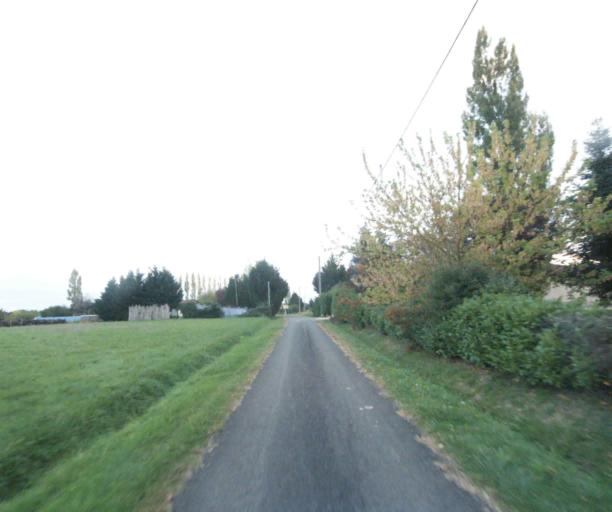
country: FR
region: Midi-Pyrenees
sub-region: Departement du Gers
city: Montreal
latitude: 43.9640
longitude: 0.1233
